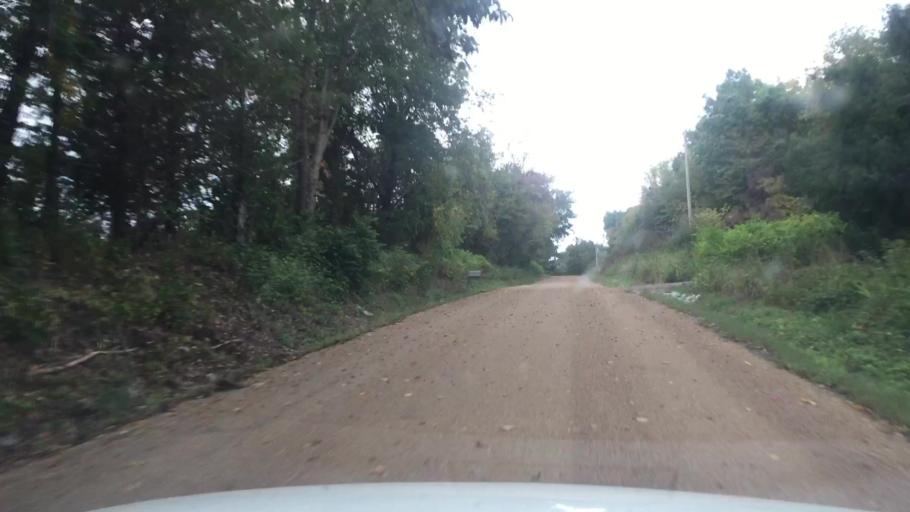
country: US
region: Missouri
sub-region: Boone County
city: Columbia
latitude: 38.8826
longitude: -92.4195
